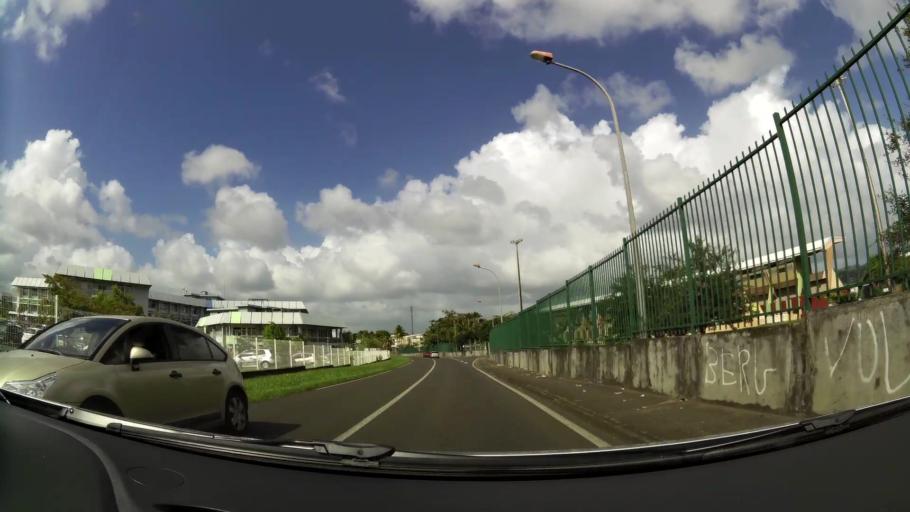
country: MQ
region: Martinique
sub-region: Martinique
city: Le Lamentin
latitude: 14.6196
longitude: -60.9879
